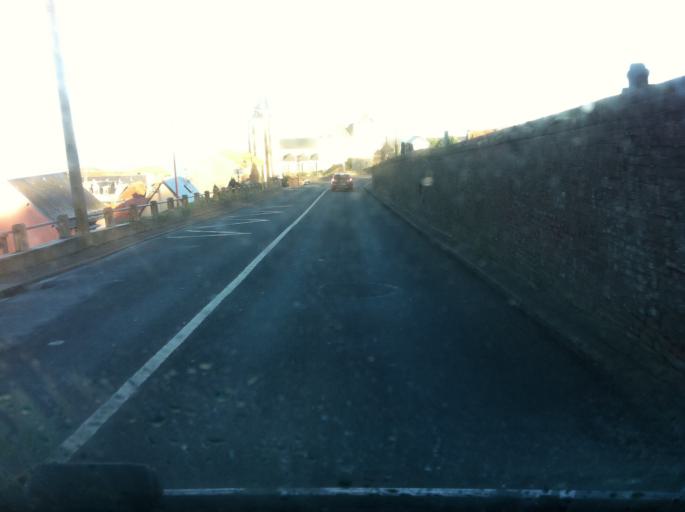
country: FR
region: Haute-Normandie
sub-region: Departement de la Seine-Maritime
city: Le Treport
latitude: 50.0577
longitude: 1.3733
